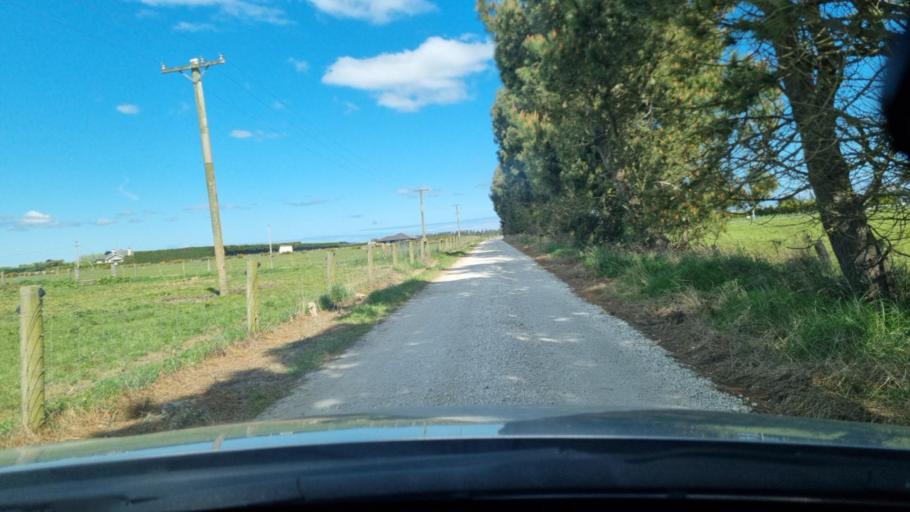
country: NZ
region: Southland
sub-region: Invercargill City
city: Invercargill
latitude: -46.3674
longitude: 168.2827
